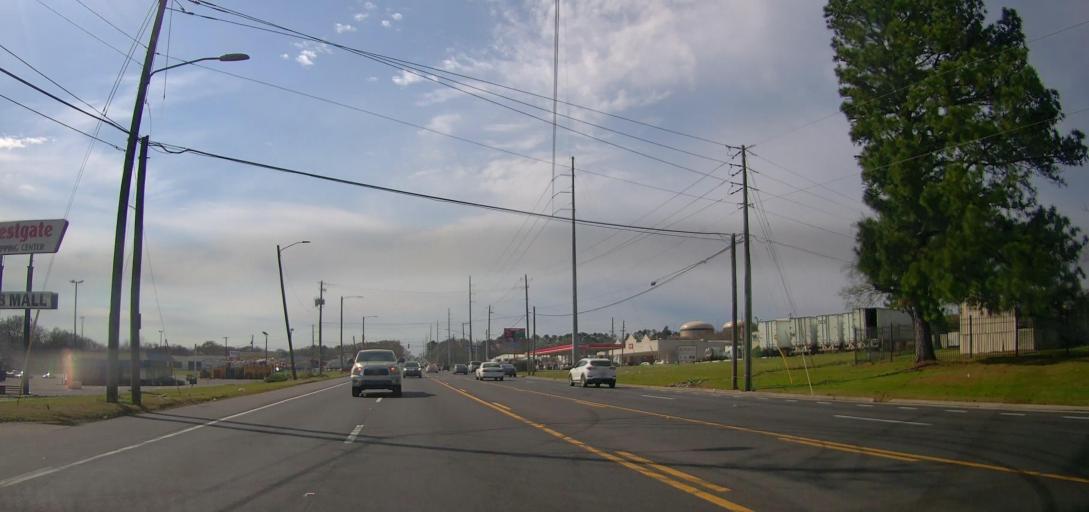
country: US
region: Alabama
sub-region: Jefferson County
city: Birmingham
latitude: 33.5321
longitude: -86.8555
